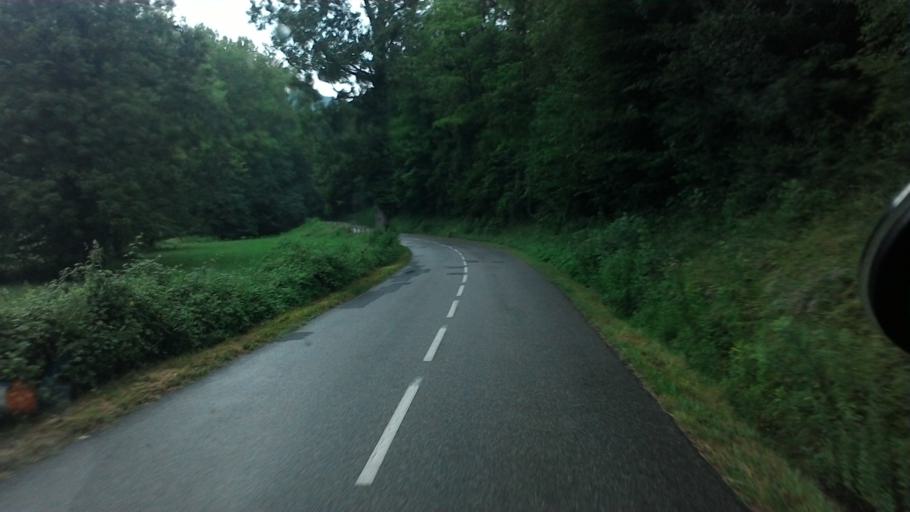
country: FR
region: Rhone-Alpes
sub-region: Departement de l'Ain
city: Belley
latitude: 45.7702
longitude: 5.6196
